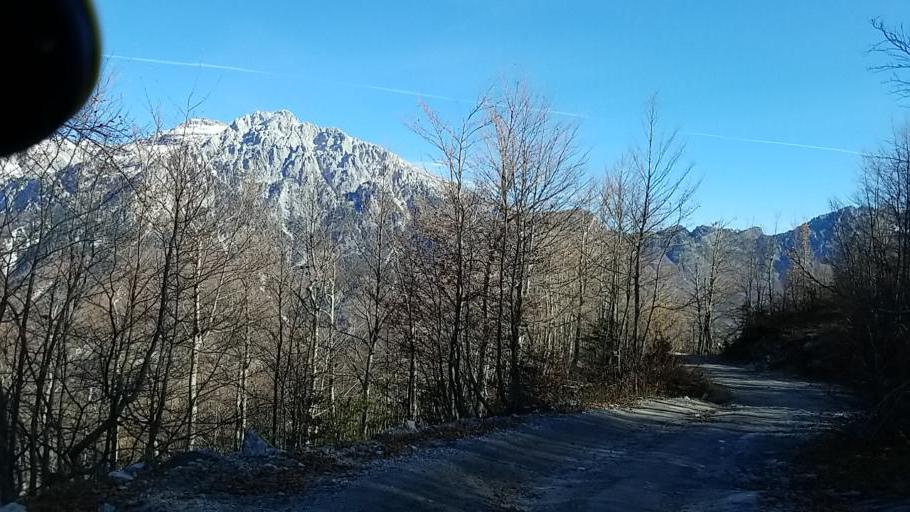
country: AL
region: Shkoder
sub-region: Rrethi i Shkodres
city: Nicaj-Shale
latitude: 42.3873
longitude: 19.7579
